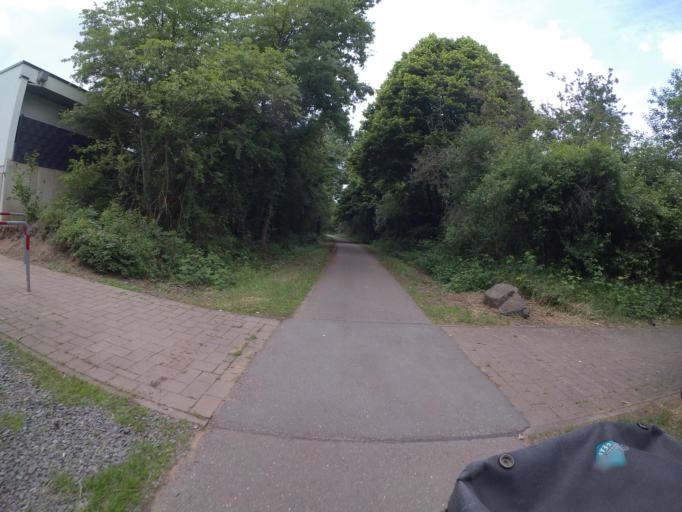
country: DE
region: Rheinland-Pfalz
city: Schwedelbach
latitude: 49.4942
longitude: 7.6012
